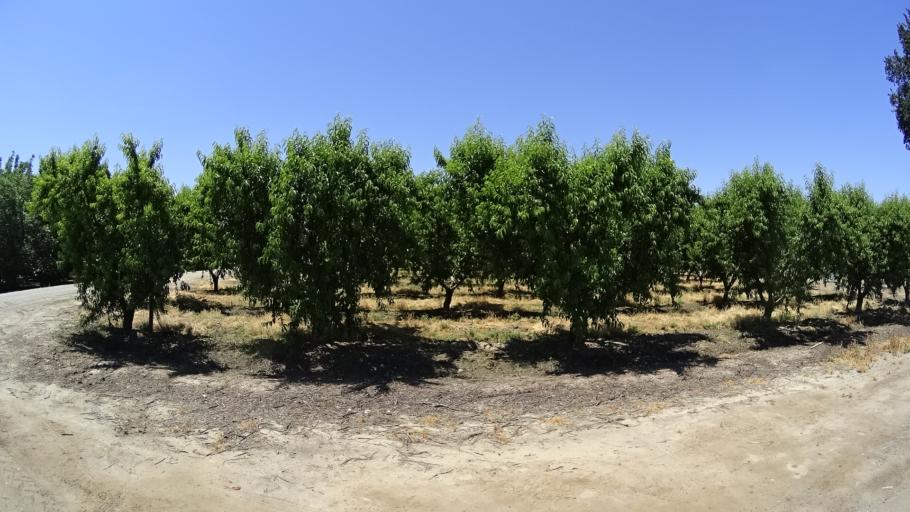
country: US
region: California
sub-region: Fresno County
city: Kingsburg
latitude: 36.4401
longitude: -119.5918
